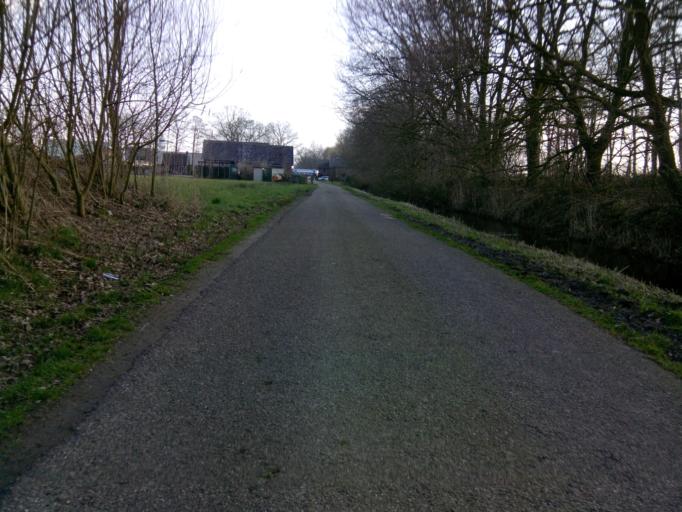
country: NL
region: Utrecht
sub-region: Gemeente Woudenberg
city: Woudenberg
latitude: 52.0890
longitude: 5.4427
